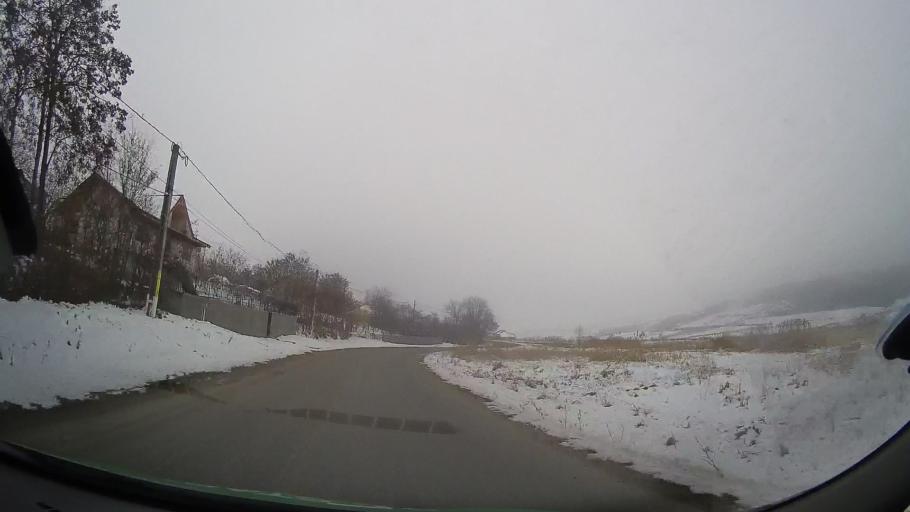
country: RO
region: Bacau
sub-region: Comuna Vultureni
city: Vultureni
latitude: 46.3519
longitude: 27.2888
